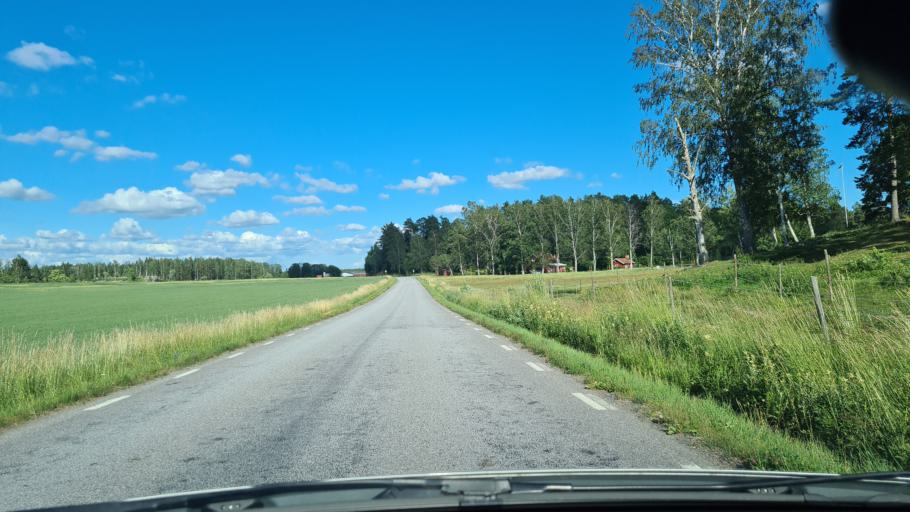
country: SE
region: Soedermanland
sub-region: Nykopings Kommun
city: Olstorp
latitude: 58.8161
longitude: 16.4780
